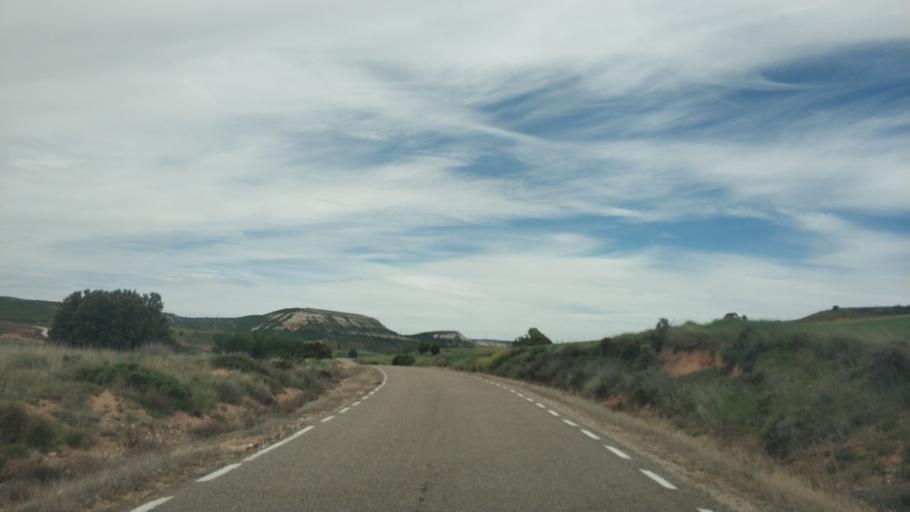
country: ES
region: Castille and Leon
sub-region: Provincia de Soria
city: Caltojar
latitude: 41.4329
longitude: -2.8031
